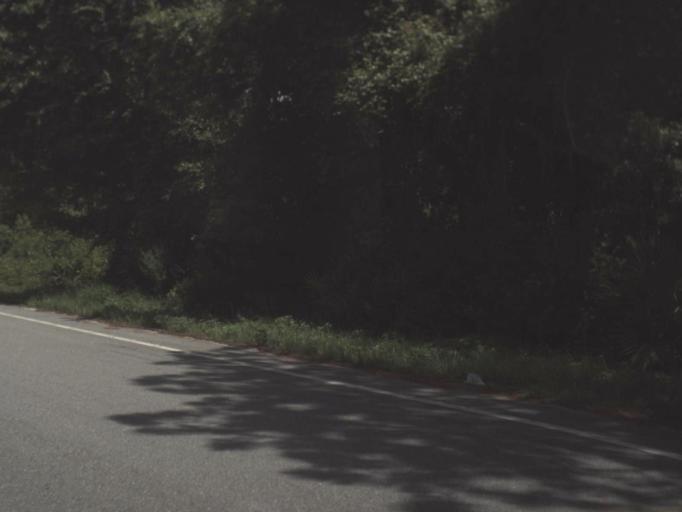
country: US
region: Florida
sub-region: Putnam County
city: Crescent City
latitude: 29.3636
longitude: -81.5075
